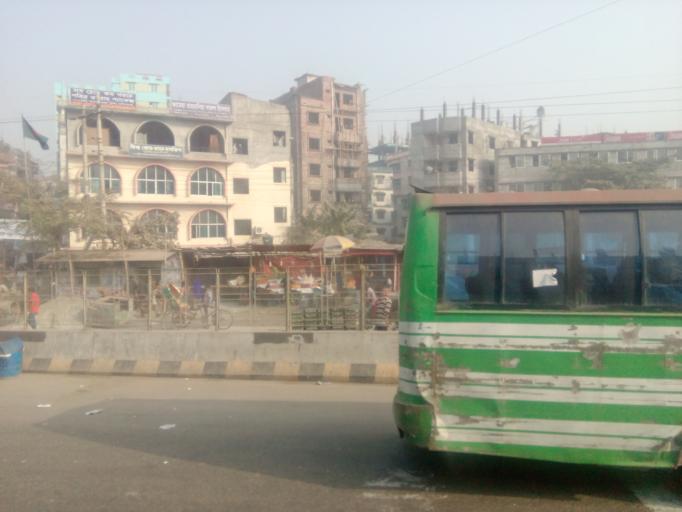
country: BD
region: Dhaka
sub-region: Dhaka
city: Dhaka
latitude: 23.7058
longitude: 90.4442
